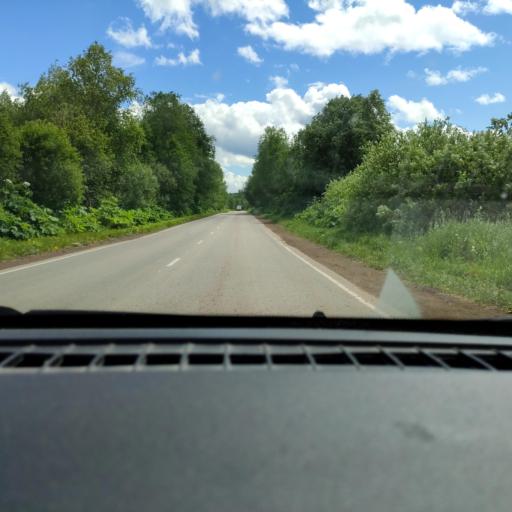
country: RU
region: Perm
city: Overyata
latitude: 58.1194
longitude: 55.8235
